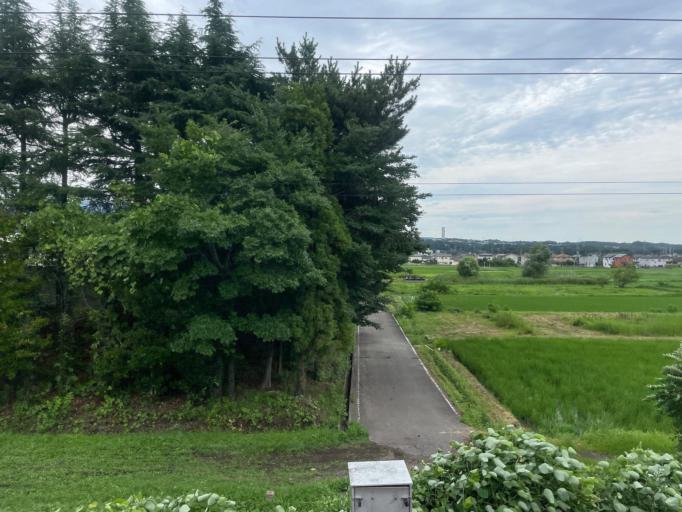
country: JP
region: Gunma
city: Shibukawa
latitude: 36.4812
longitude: 139.0070
